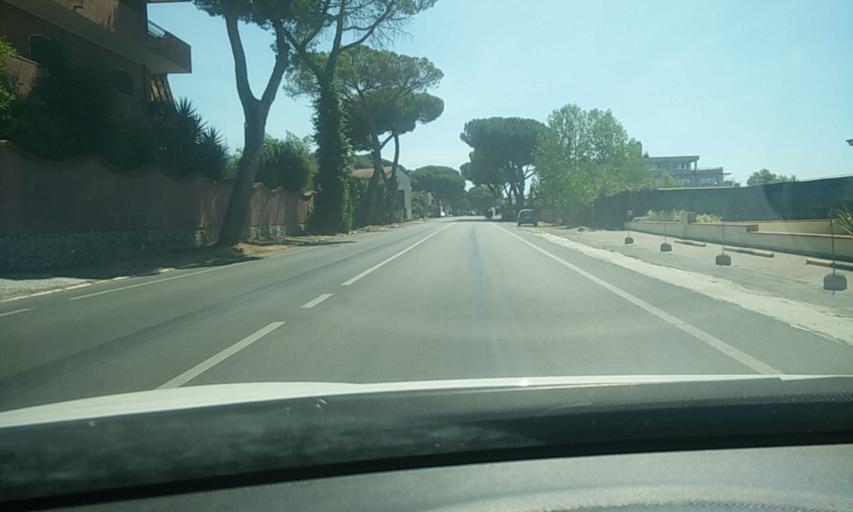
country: IT
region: Tuscany
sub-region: Provincia di Massa-Carrara
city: Carrara
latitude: 44.0429
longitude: 10.0878
